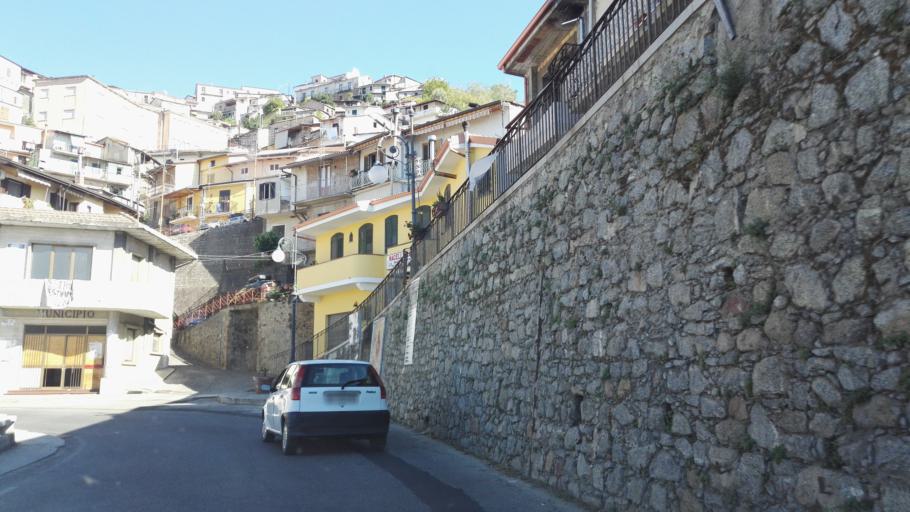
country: IT
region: Calabria
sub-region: Provincia di Vibo-Valentia
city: Sorianello
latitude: 38.5924
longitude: 16.2312
